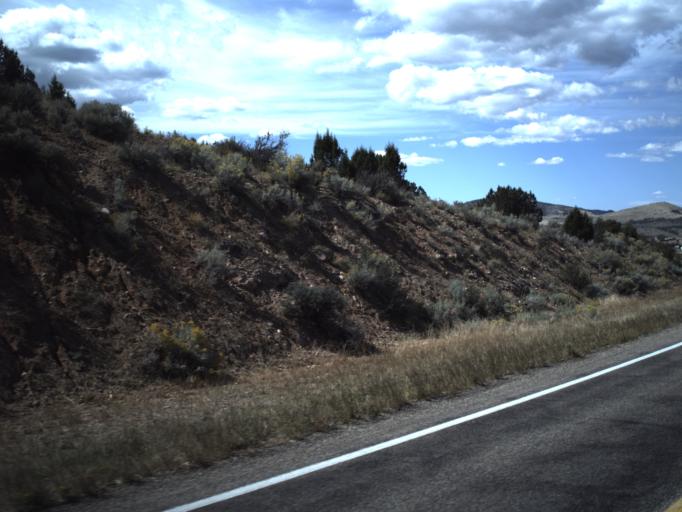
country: US
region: Utah
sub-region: Washington County
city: Enterprise
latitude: 37.5651
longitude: -113.6927
